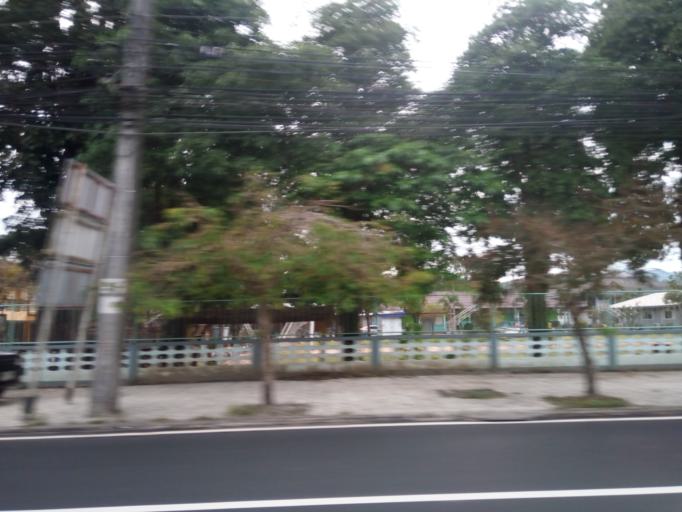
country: TH
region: Phuket
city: Ban Ko Kaeo
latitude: 7.9770
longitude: 98.3681
